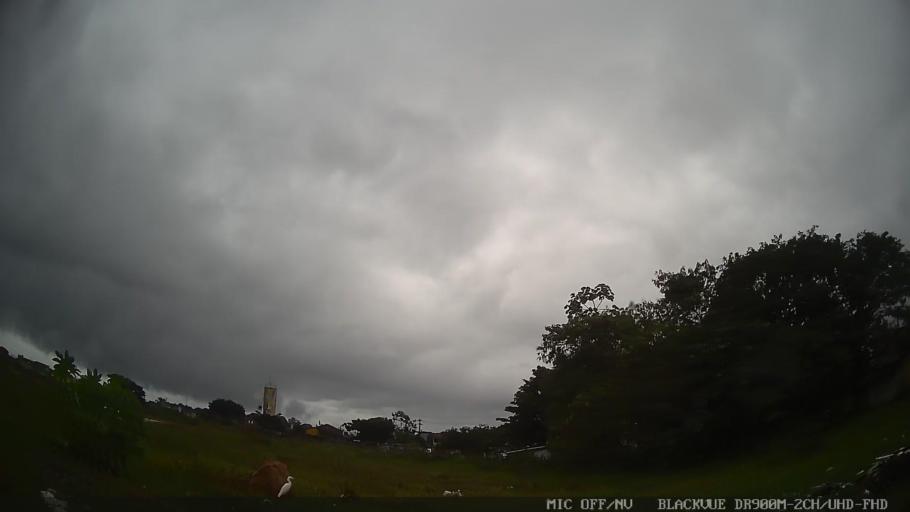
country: BR
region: Sao Paulo
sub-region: Itanhaem
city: Itanhaem
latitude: -24.1839
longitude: -46.8285
